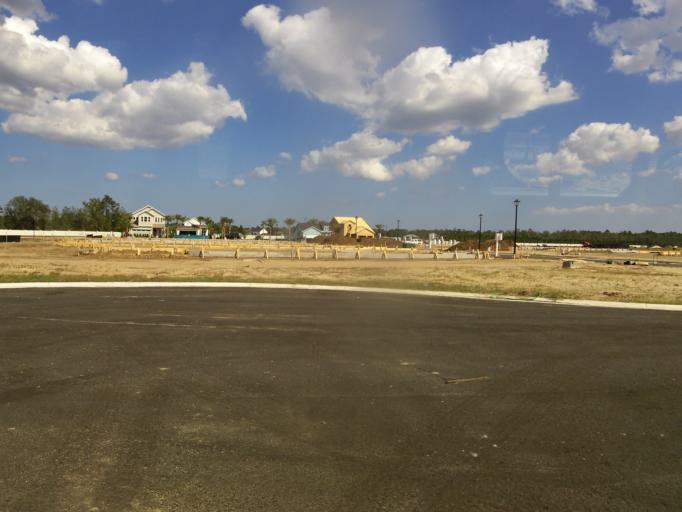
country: US
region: Florida
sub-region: Saint Johns County
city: Palm Valley
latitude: 30.1917
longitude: -81.5075
